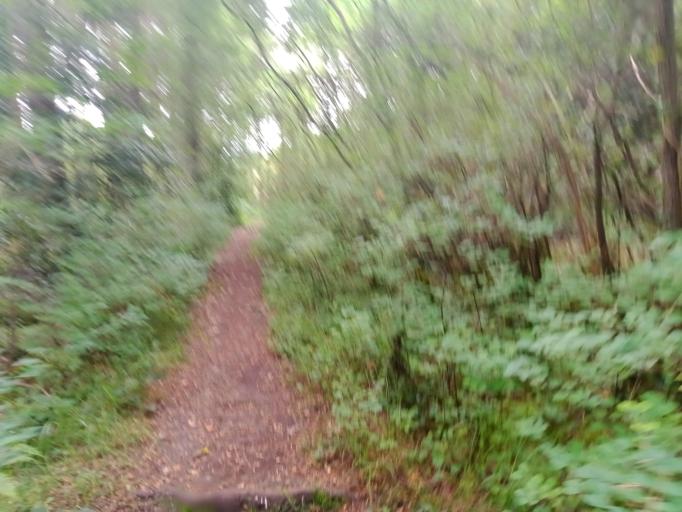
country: IE
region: Leinster
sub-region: Laois
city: Abbeyleix
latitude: 52.8845
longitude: -7.3571
